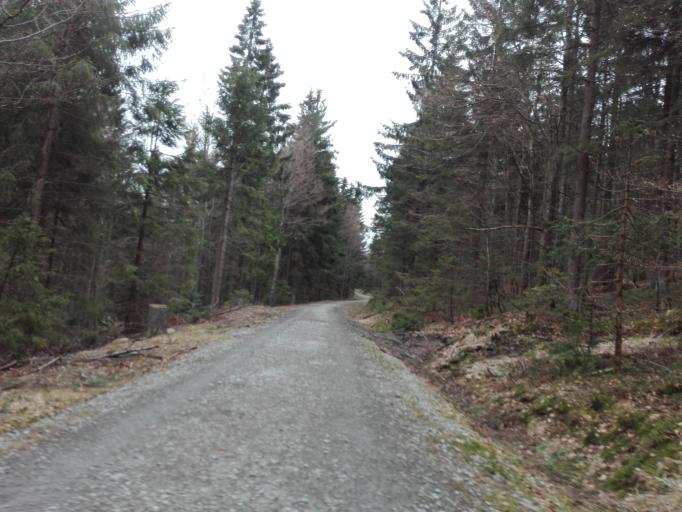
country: AT
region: Upper Austria
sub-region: Politischer Bezirk Rohrbach
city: Aigen im Muehlkreis
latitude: 48.7038
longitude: 13.9667
